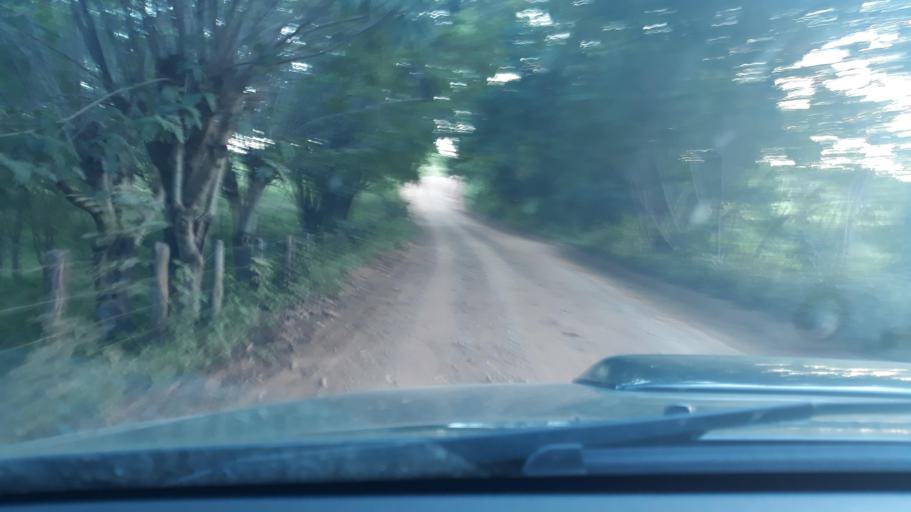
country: BR
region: Bahia
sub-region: Riacho De Santana
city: Riacho de Santana
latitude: -13.8130
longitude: -42.7212
